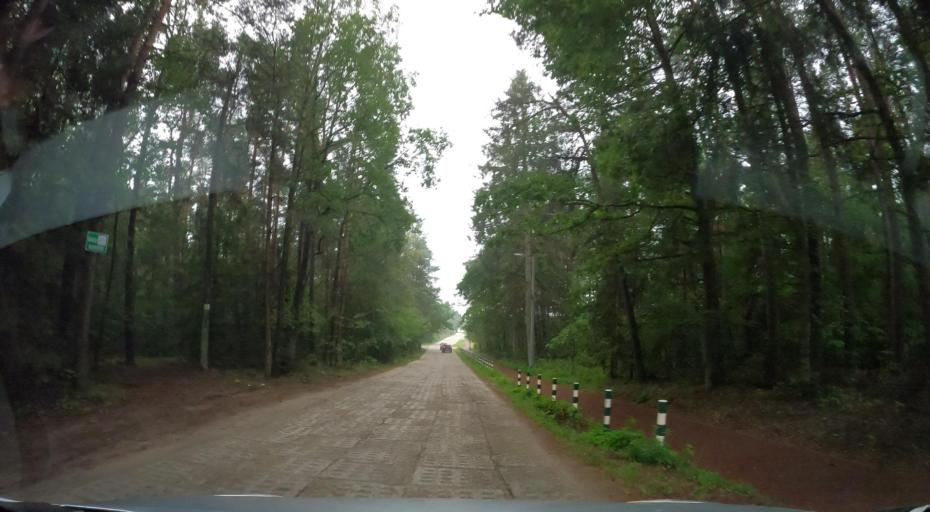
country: PL
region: Pomeranian Voivodeship
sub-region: Powiat kartuski
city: Chwaszczyno
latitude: 54.4334
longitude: 18.4178
